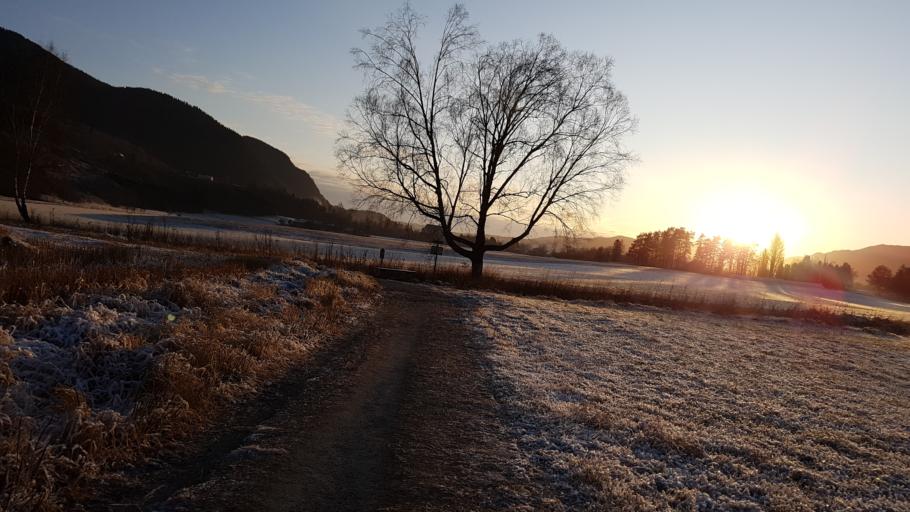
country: NO
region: Sor-Trondelag
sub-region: Melhus
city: Melhus
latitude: 63.2838
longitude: 10.2986
